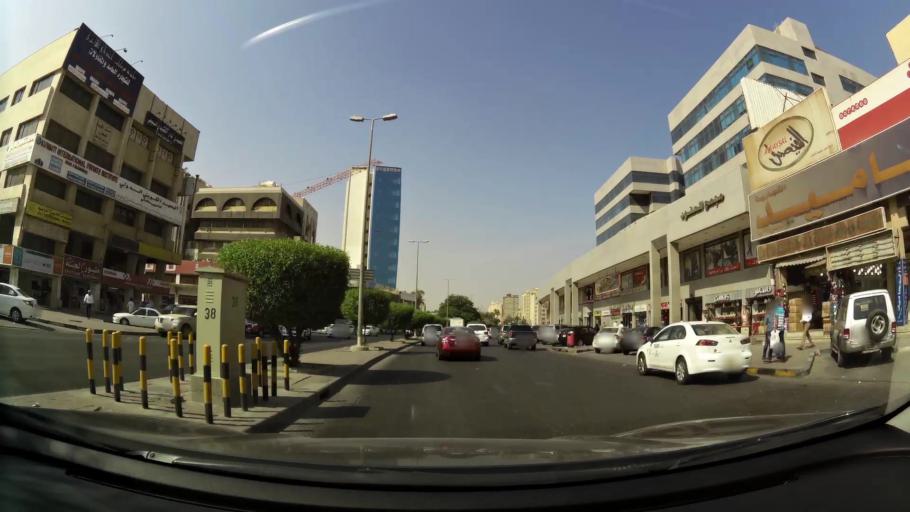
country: KW
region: Al Ahmadi
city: Al Fahahil
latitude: 29.0799
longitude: 48.1349
